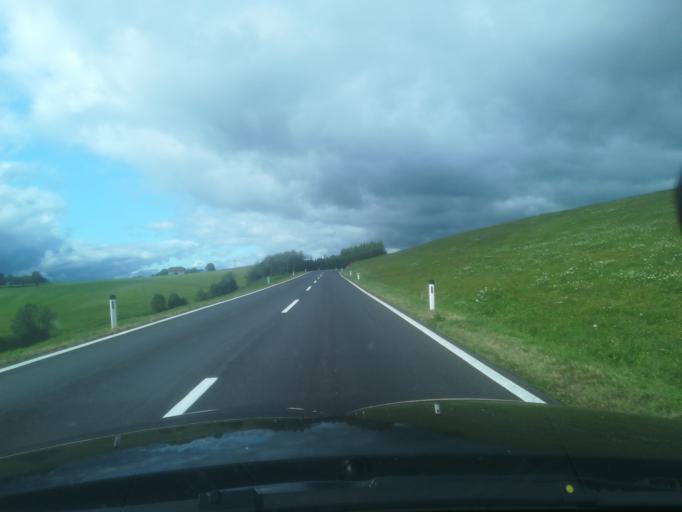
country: AT
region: Upper Austria
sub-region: Politischer Bezirk Urfahr-Umgebung
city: Gramastetten
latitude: 48.4092
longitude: 14.1700
